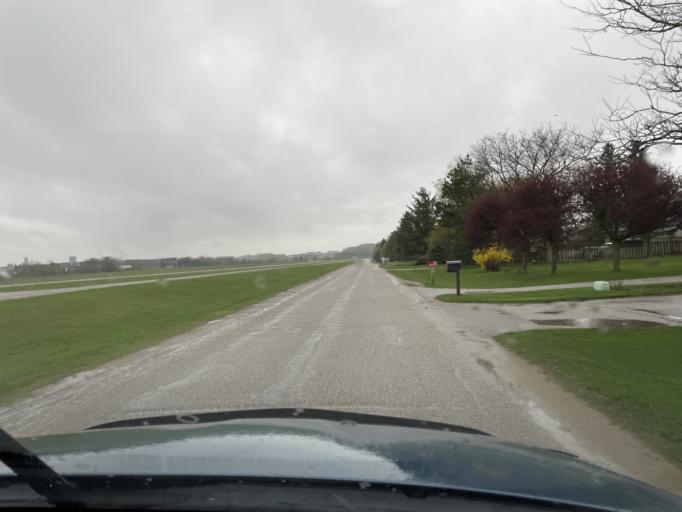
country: CA
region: Ontario
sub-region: Wellington County
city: Guelph
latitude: 43.5644
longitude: -80.1967
